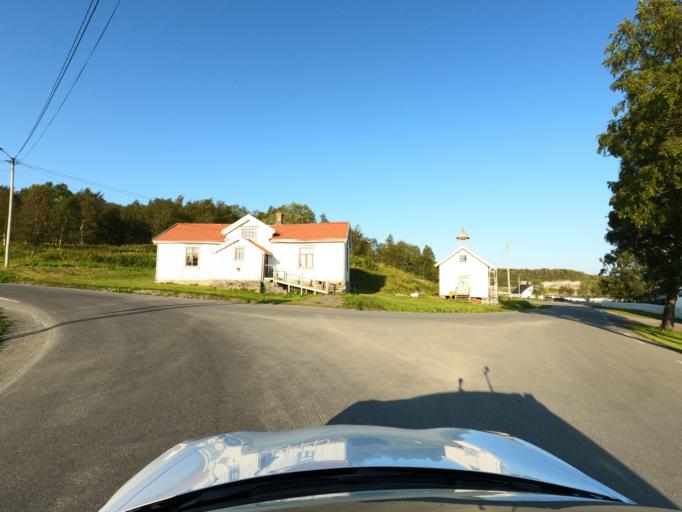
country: NO
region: Nordland
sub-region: Ballangen
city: Ballangen
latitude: 68.4587
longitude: 16.6992
